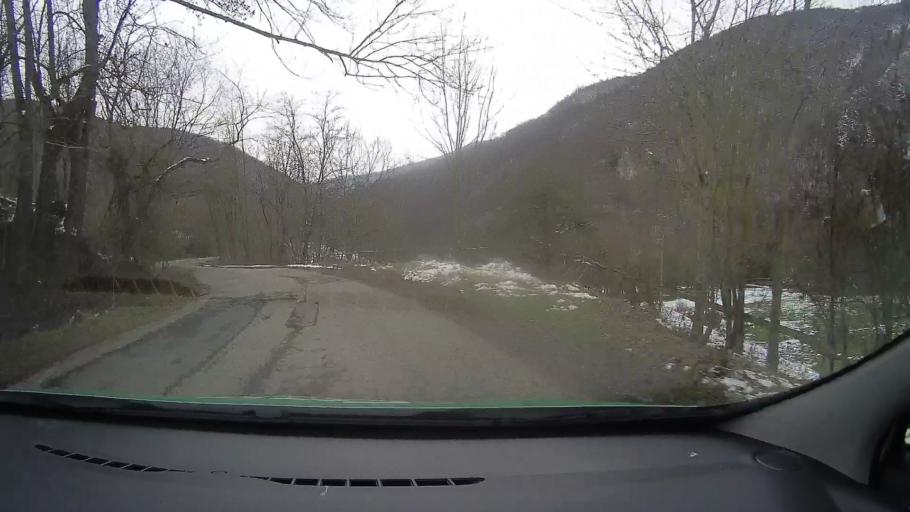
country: RO
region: Hunedoara
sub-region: Comuna Balsa
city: Balsa
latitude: 46.0165
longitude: 23.1488
